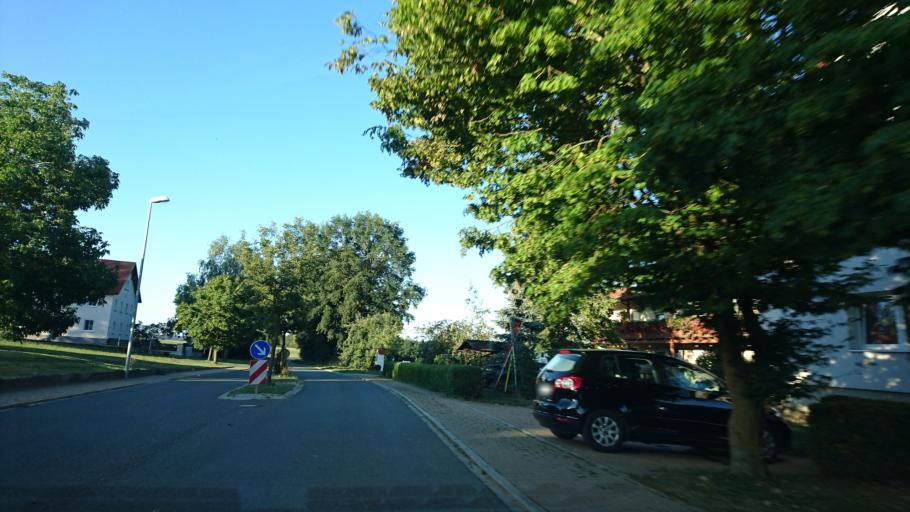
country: DE
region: Bavaria
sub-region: Regierungsbezirk Mittelfranken
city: Nennslingen
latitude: 49.0568
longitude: 11.1677
